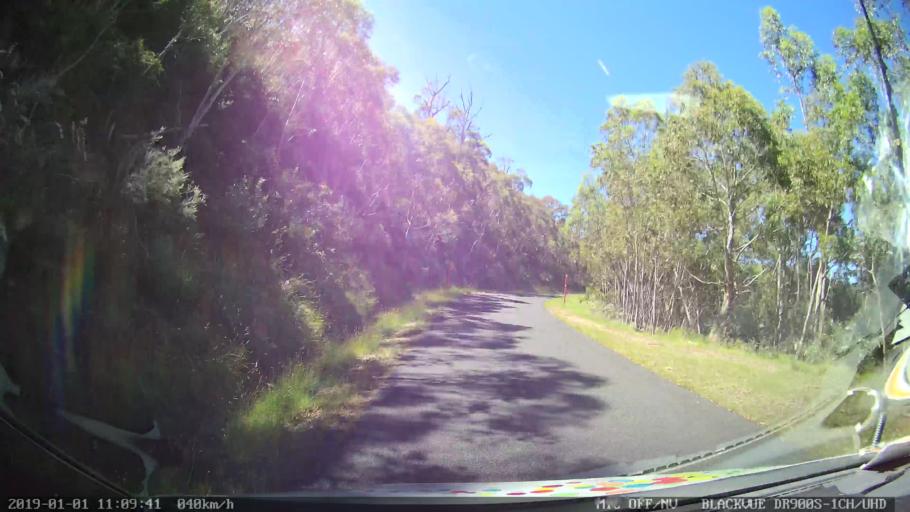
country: AU
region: New South Wales
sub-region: Snowy River
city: Jindabyne
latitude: -35.9655
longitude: 148.3993
